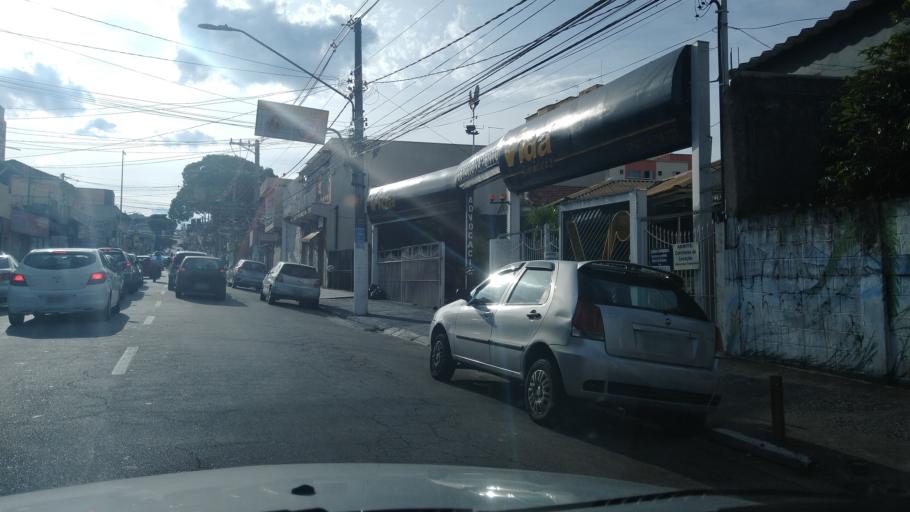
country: BR
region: Sao Paulo
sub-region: Osasco
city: Osasco
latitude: -23.5313
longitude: -46.7986
